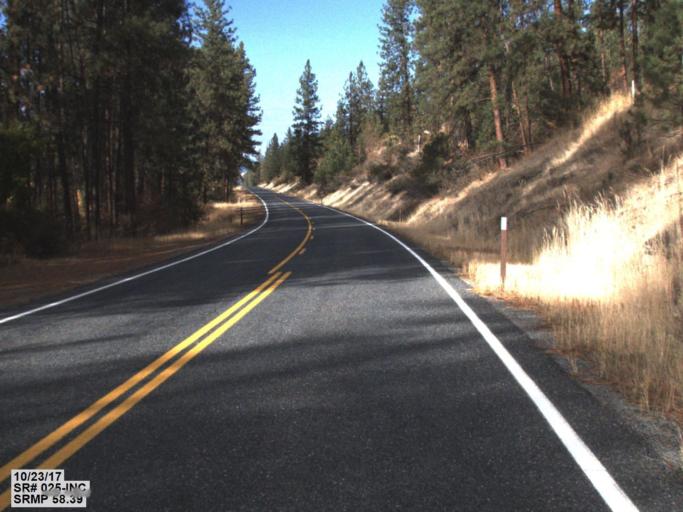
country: US
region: Washington
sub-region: Stevens County
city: Kettle Falls
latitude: 48.3159
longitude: -118.1486
